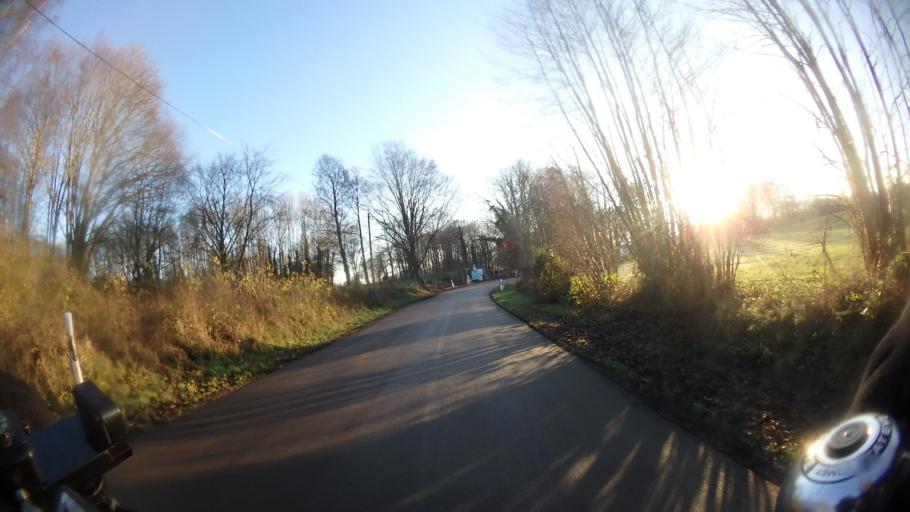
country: DE
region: Schleswig-Holstein
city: Travemuende
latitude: 53.9850
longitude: 10.8724
